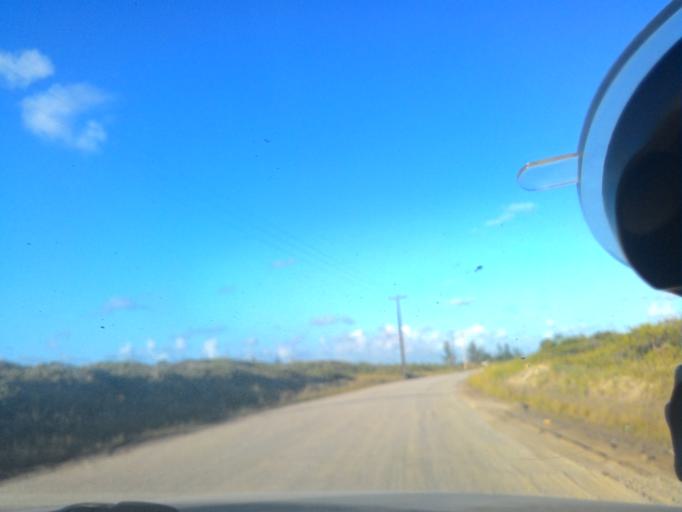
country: BR
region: Sao Paulo
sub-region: Pariquera-Acu
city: Pariquera Acu
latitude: -24.8680
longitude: -47.7193
